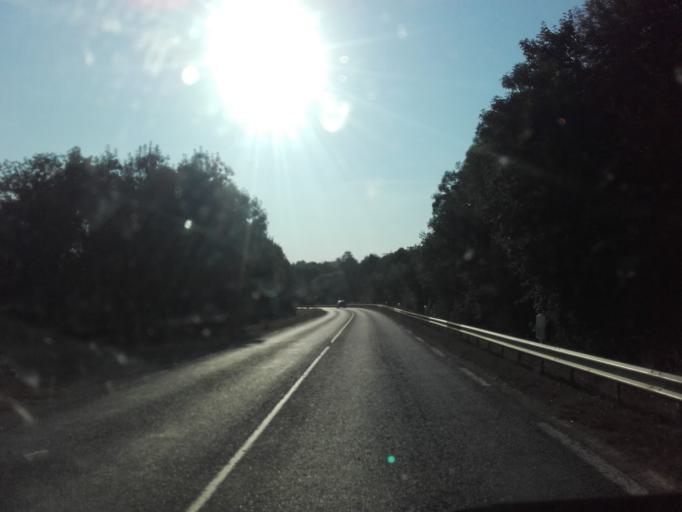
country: FR
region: Bourgogne
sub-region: Departement de l'Yonne
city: Venoy
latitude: 47.7932
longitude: 3.6199
